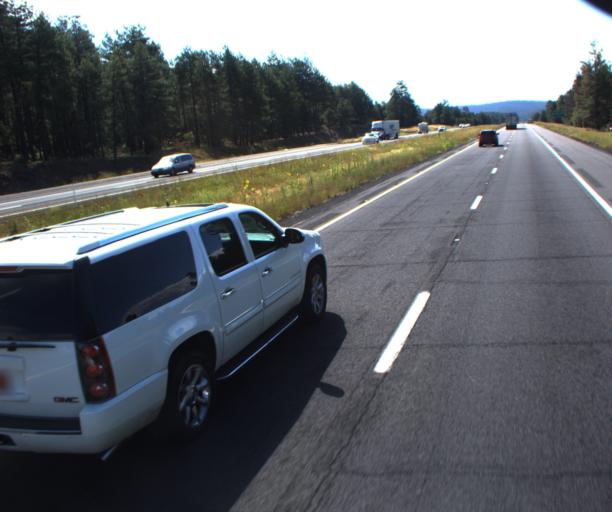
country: US
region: Arizona
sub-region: Coconino County
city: Sedona
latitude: 34.9550
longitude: -111.6746
